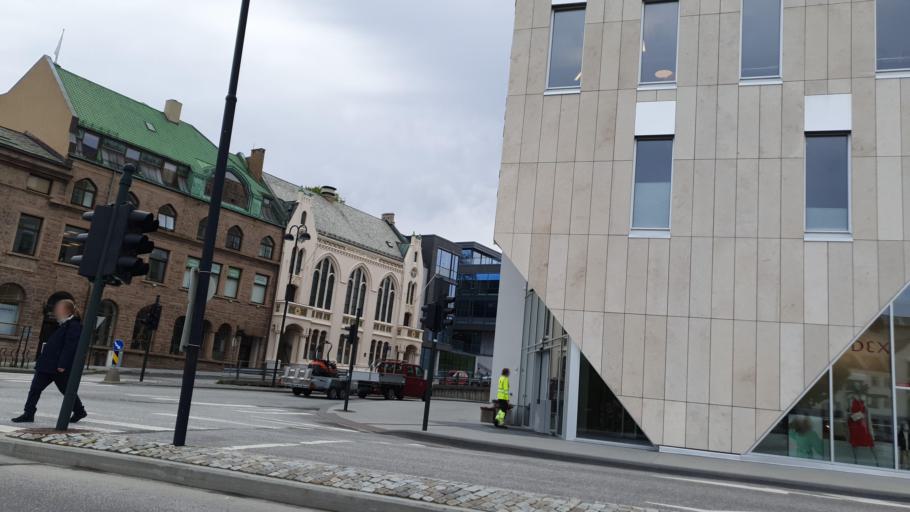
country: NO
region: More og Romsdal
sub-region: Alesund
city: Alesund
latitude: 62.4721
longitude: 6.1546
